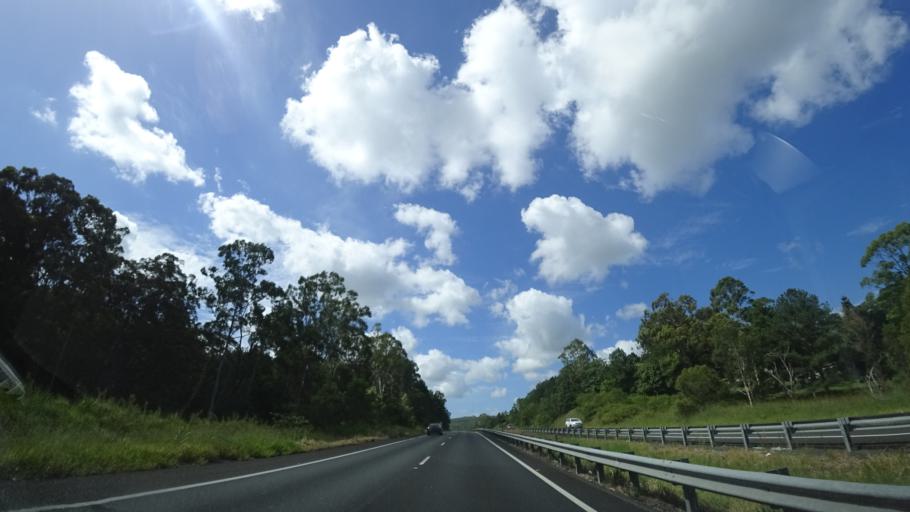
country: AU
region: Queensland
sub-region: Sunshine Coast
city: Twin Waters
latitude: -26.6284
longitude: 152.9880
